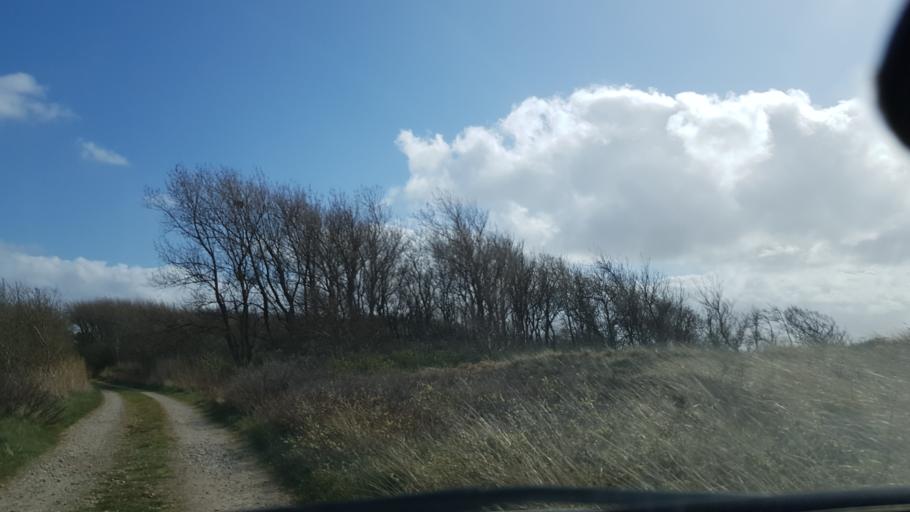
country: DE
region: Schleswig-Holstein
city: List
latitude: 55.0803
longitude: 8.5398
